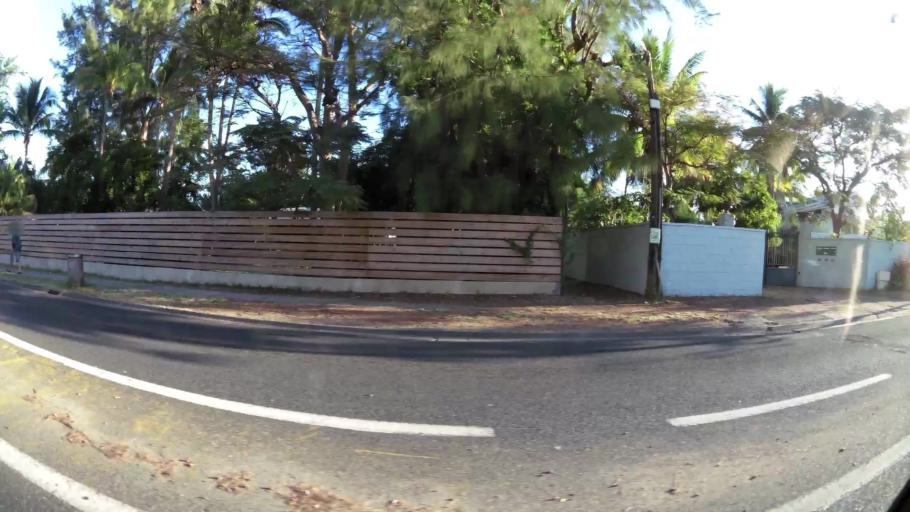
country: RE
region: Reunion
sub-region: Reunion
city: Trois-Bassins
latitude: -21.0961
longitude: 55.2387
